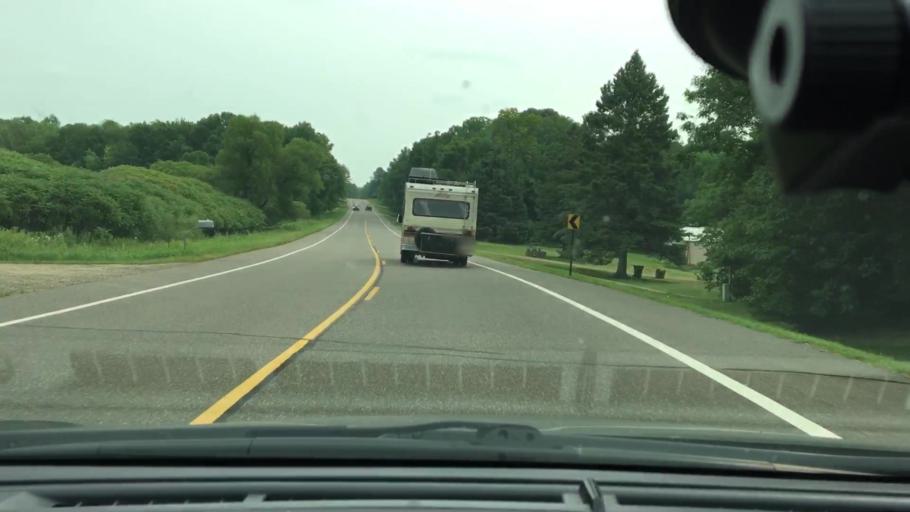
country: US
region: Minnesota
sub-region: Crow Wing County
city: Crosby
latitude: 46.4079
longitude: -93.8208
